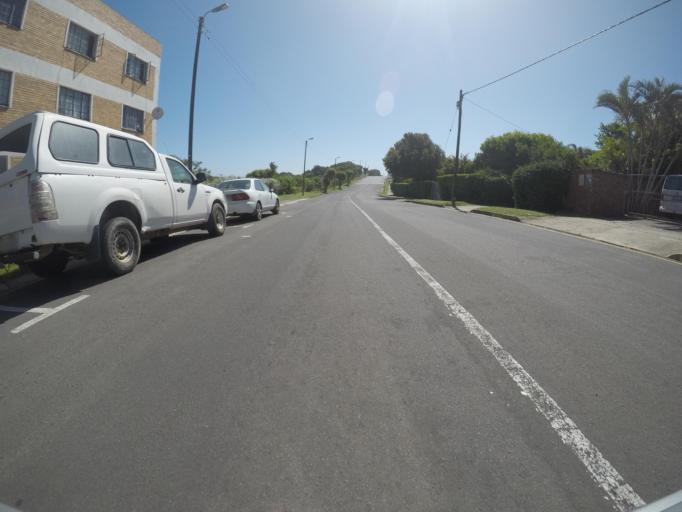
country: ZA
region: Eastern Cape
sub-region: Buffalo City Metropolitan Municipality
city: East London
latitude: -32.9886
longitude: 27.9436
